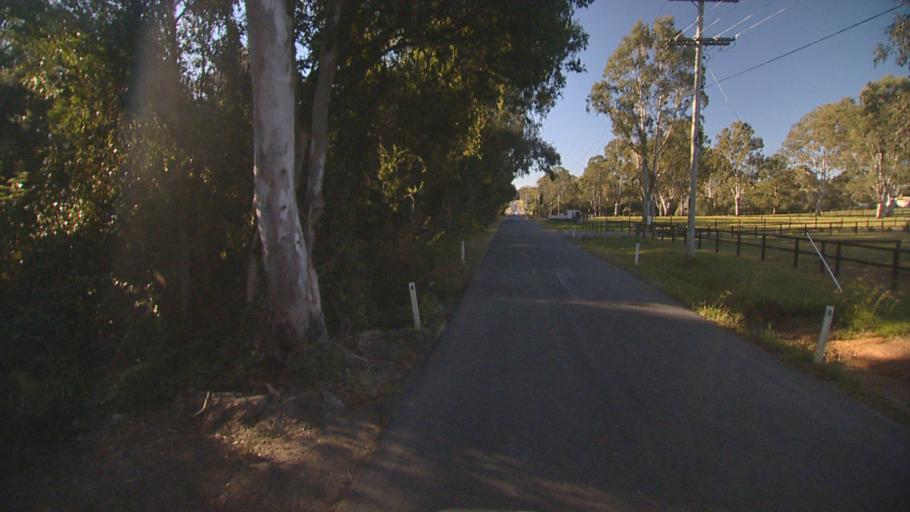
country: AU
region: Queensland
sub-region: Logan
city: Logan Reserve
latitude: -27.7575
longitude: 153.1400
